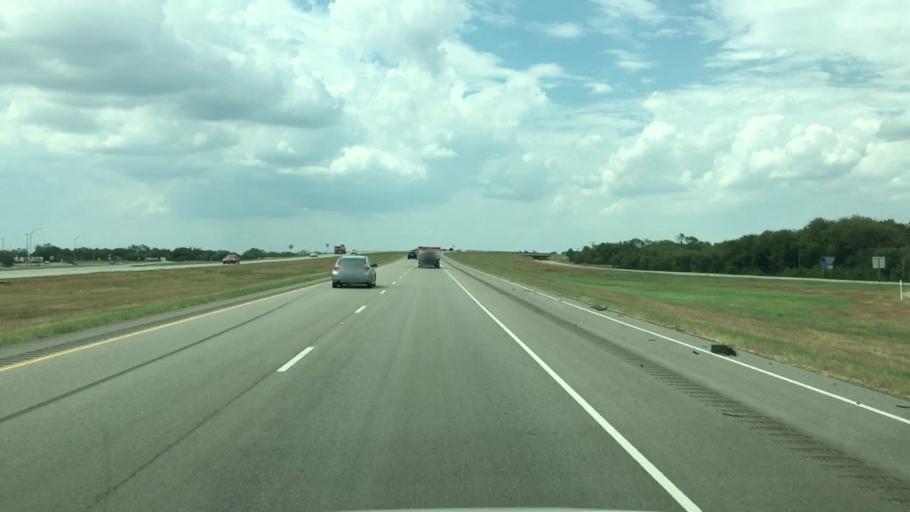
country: US
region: Texas
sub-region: Live Oak County
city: Three Rivers
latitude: 28.5208
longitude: -98.1809
